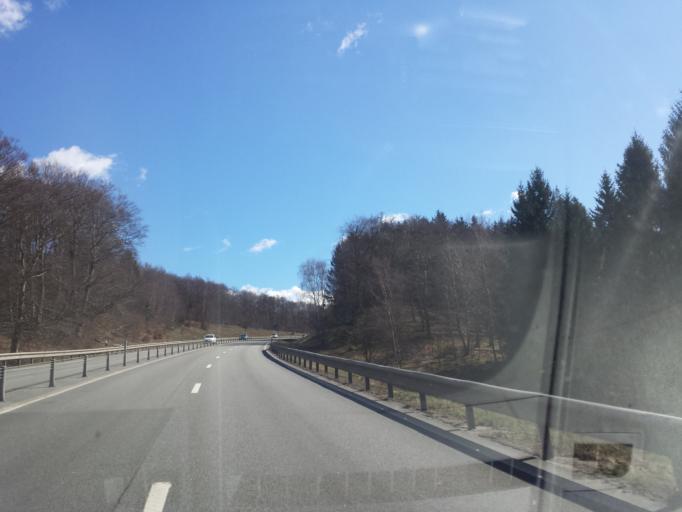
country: SE
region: Skane
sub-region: Sjobo Kommun
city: Sjoebo
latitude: 55.6230
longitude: 13.7239
